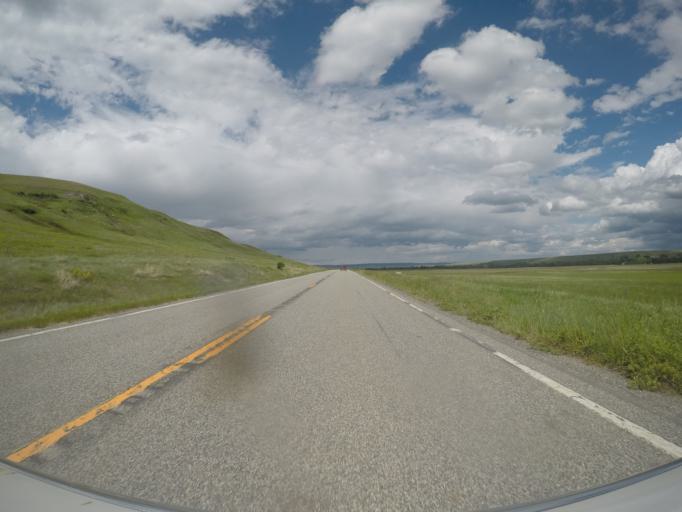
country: US
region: Montana
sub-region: Sweet Grass County
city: Big Timber
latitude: 45.7845
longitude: -109.9825
